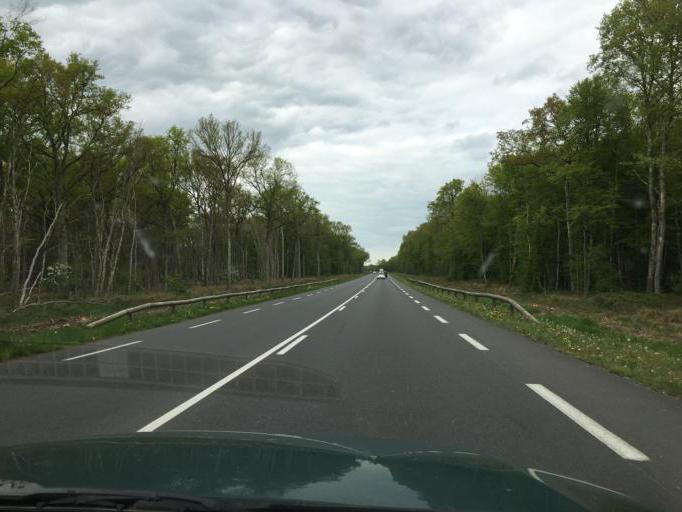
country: FR
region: Centre
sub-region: Departement du Loiret
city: Chanteau
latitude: 47.9773
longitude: 1.9328
